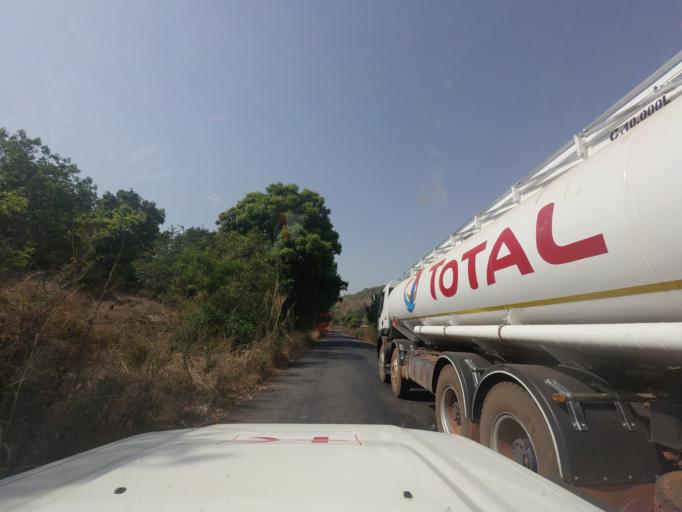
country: GN
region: Kindia
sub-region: Kindia
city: Kindia
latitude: 10.1781
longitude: -12.4676
